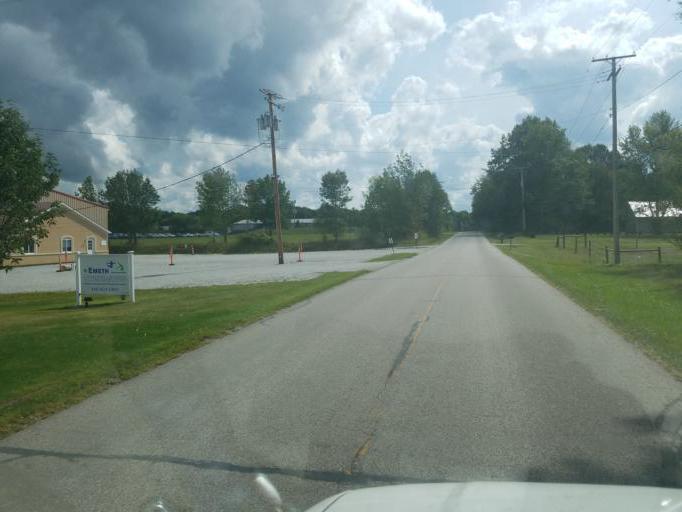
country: US
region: Ohio
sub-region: Geauga County
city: Middlefield
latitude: 41.4613
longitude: -81.1087
